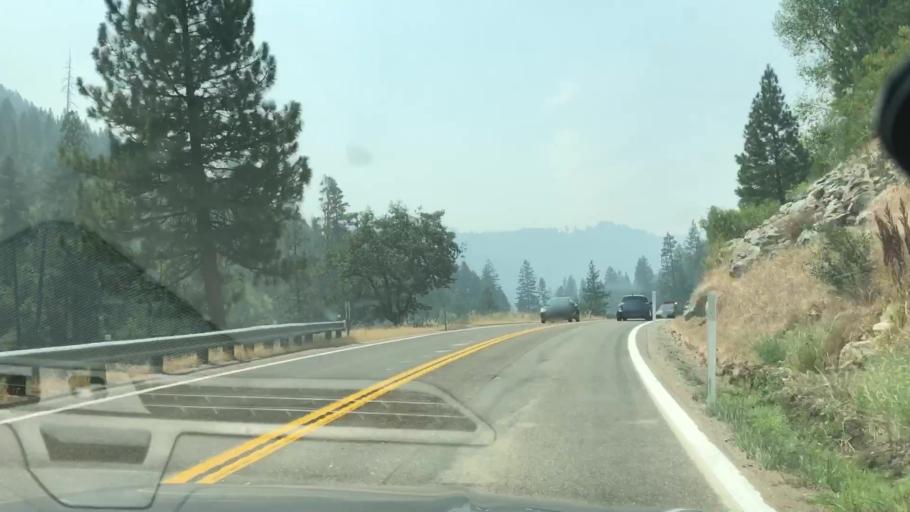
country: US
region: California
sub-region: El Dorado County
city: Pollock Pines
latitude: 38.7742
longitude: -120.4243
